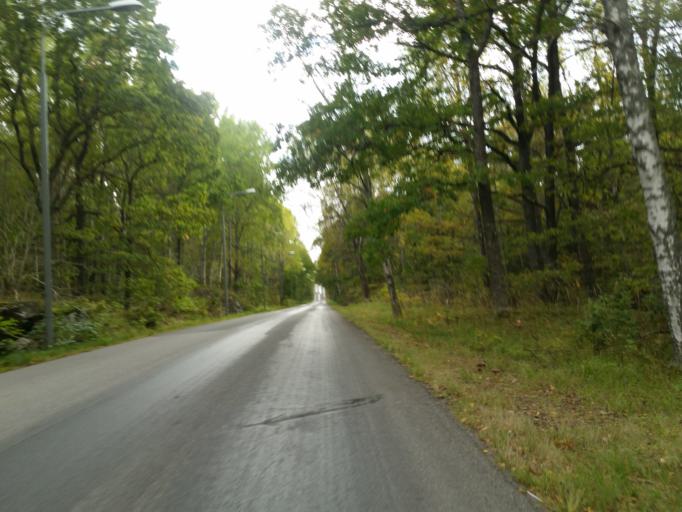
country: SE
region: Stockholm
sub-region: Nacka Kommun
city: Alta
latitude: 59.2543
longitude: 18.1360
